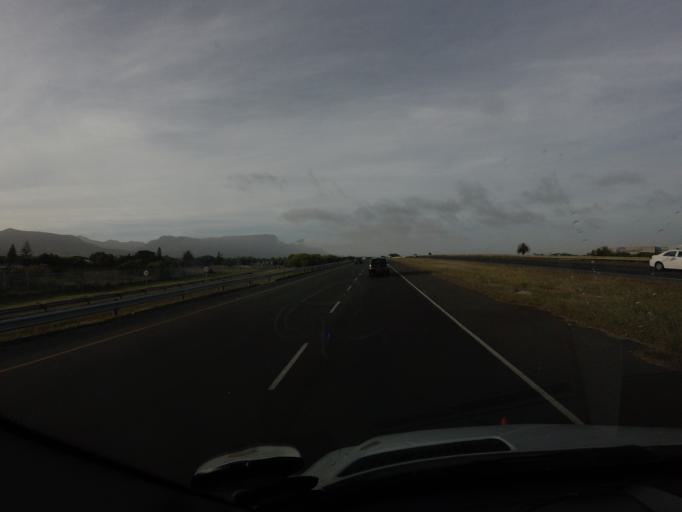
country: ZA
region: Western Cape
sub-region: City of Cape Town
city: Bergvliet
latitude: -34.0665
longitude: 18.4484
